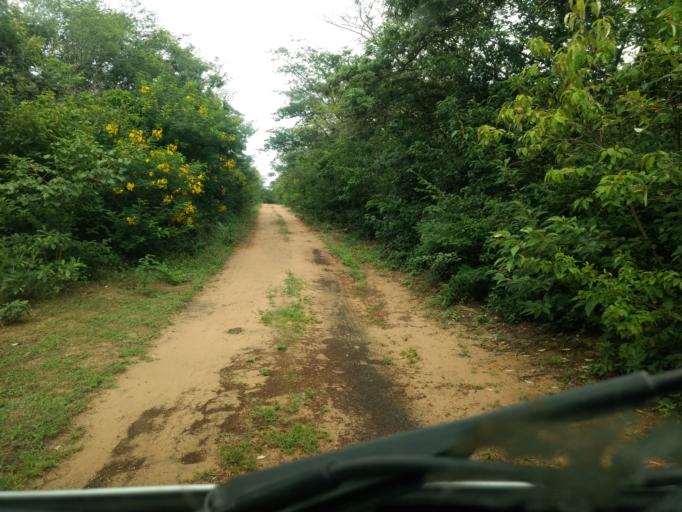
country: BR
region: Ceara
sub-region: Crateus
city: Crateus
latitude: -5.1816
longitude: -40.9403
